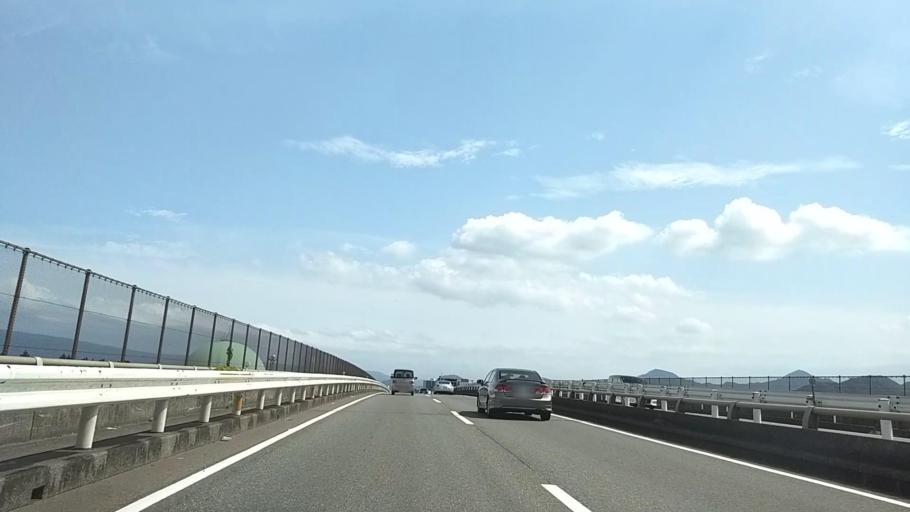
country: JP
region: Shizuoka
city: Mishima
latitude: 35.1171
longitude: 138.8888
